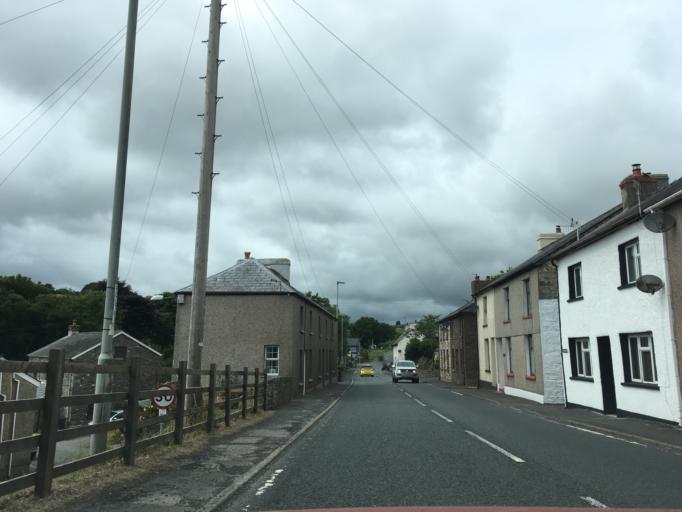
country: GB
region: Wales
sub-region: Sir Powys
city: Cray
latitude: 51.9497
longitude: -3.6301
